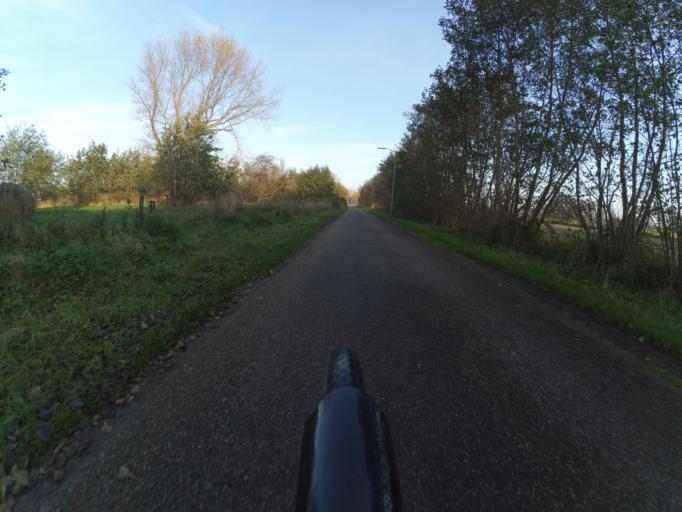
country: NL
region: South Holland
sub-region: Gemeente Goeree-Overflakkee
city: Goedereede
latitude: 51.8332
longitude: 3.9759
